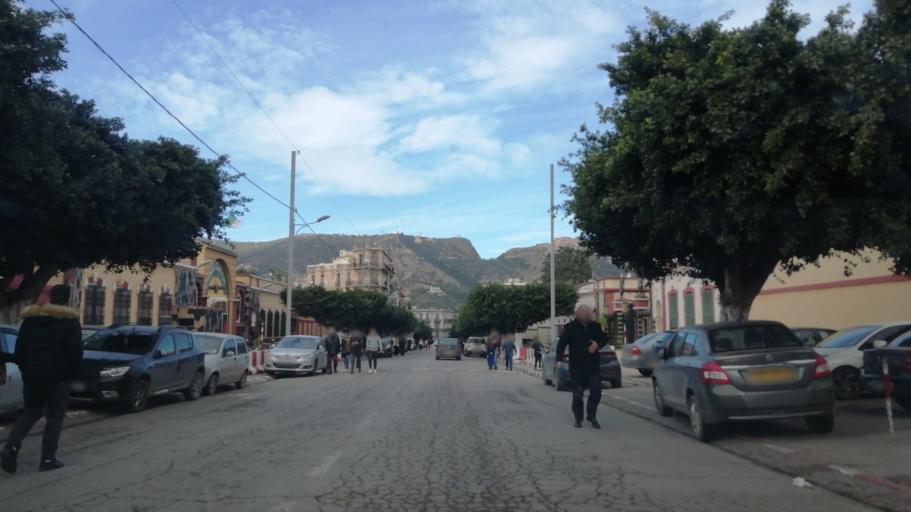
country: DZ
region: Oran
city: Oran
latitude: 35.6968
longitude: -0.6485
